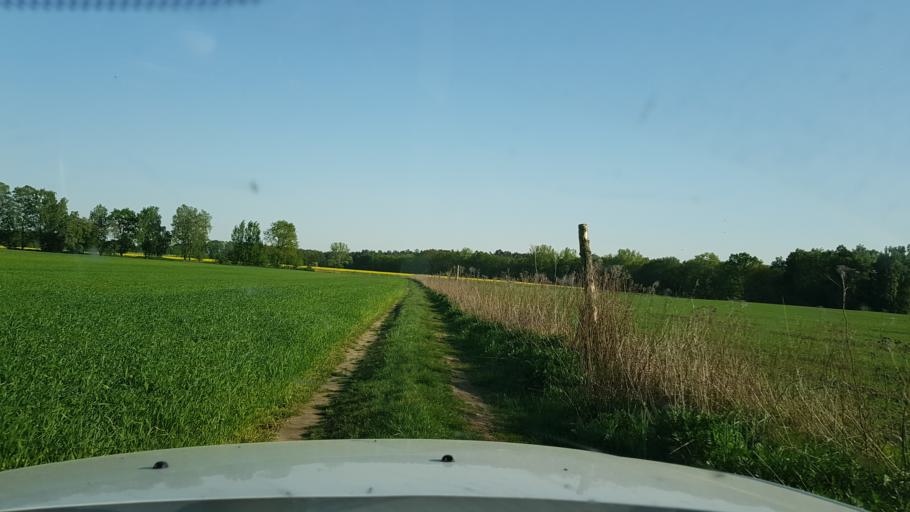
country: PL
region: West Pomeranian Voivodeship
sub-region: Powiat lobeski
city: Dobra
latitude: 53.6867
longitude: 15.3359
